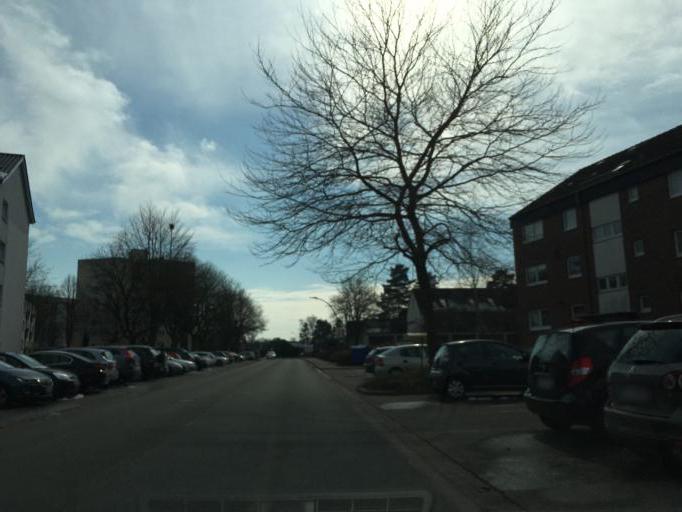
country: DE
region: Schleswig-Holstein
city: Bad Segeberg
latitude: 53.9428
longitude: 10.2954
